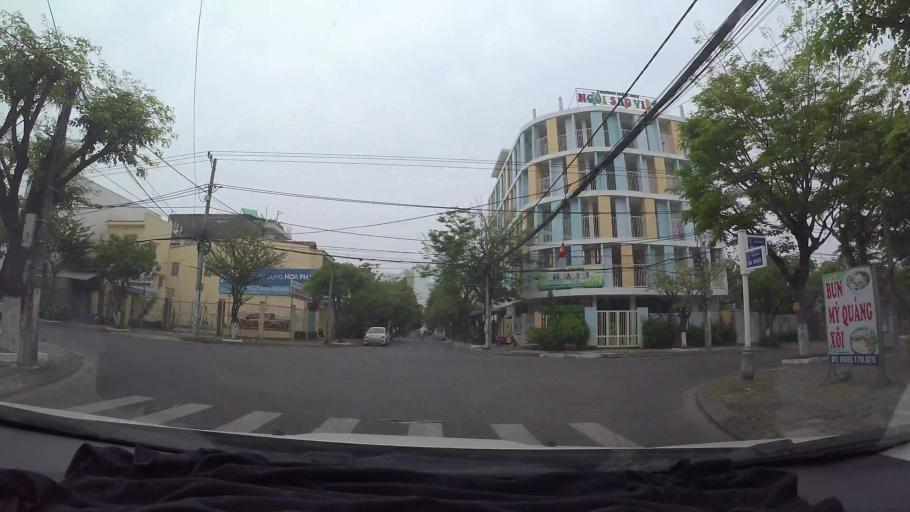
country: VN
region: Da Nang
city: Cam Le
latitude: 16.0391
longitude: 108.2140
